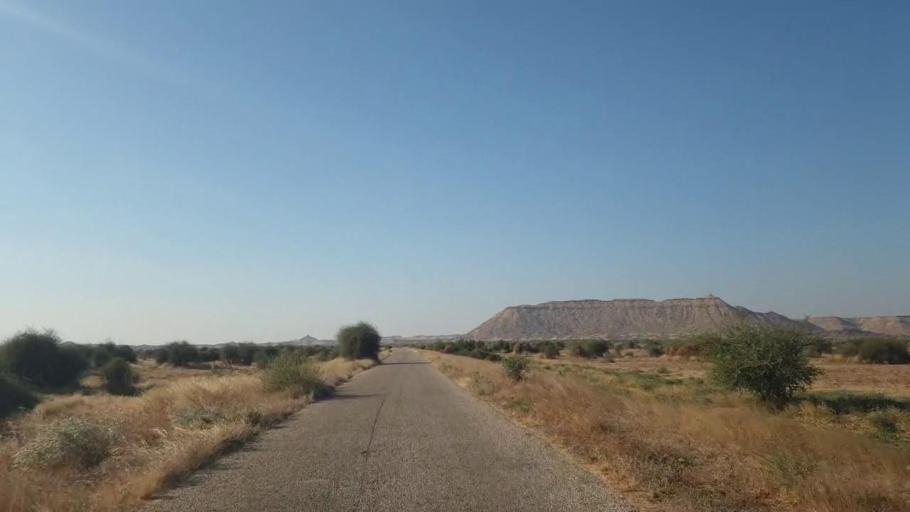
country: PK
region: Sindh
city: Malir Cantonment
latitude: 25.3900
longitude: 67.5167
